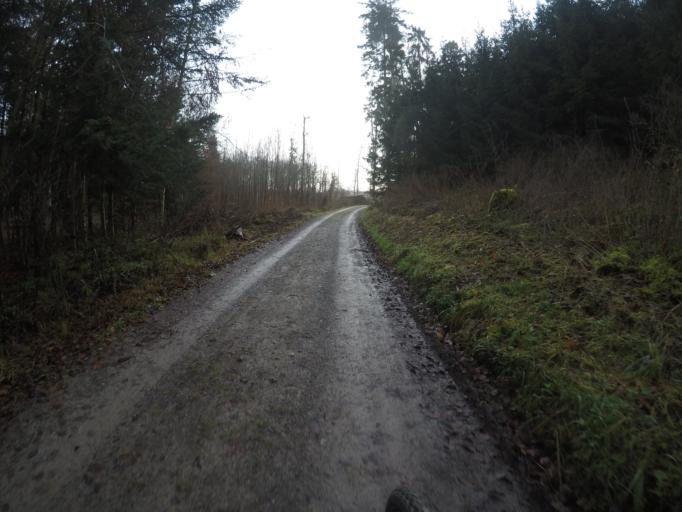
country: DE
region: Baden-Wuerttemberg
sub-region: Regierungsbezirk Stuttgart
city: Deckenpfronn
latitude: 48.6604
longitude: 8.8234
